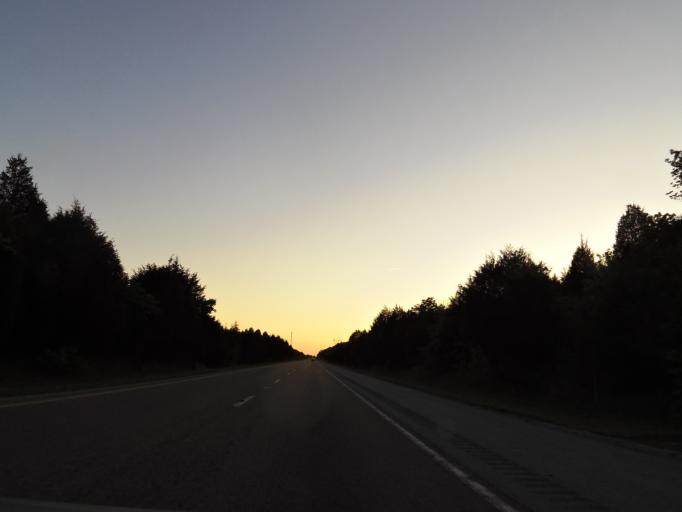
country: US
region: Tennessee
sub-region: Greene County
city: Mosheim
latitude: 36.2037
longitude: -83.1057
